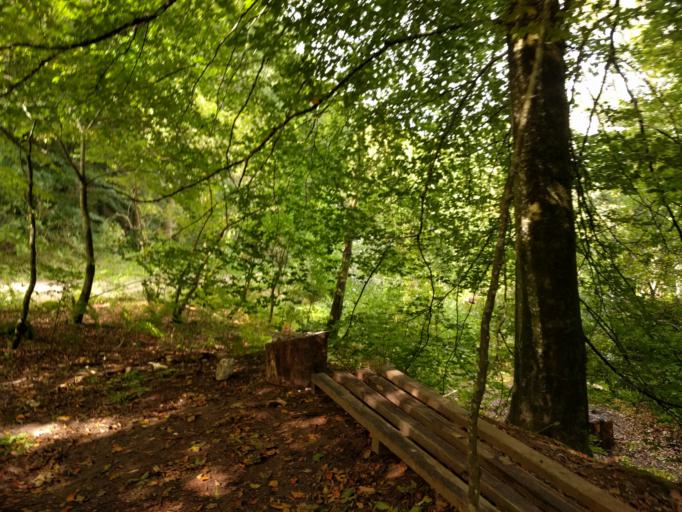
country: DK
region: Central Jutland
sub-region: Viborg Kommune
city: Stoholm
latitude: 56.4426
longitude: 9.1417
